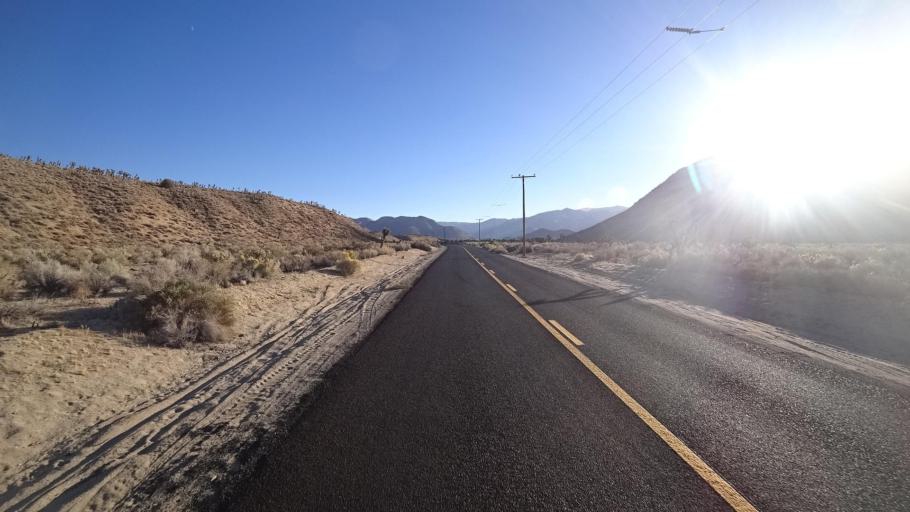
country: US
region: California
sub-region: Kern County
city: Weldon
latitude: 35.6181
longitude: -118.2435
